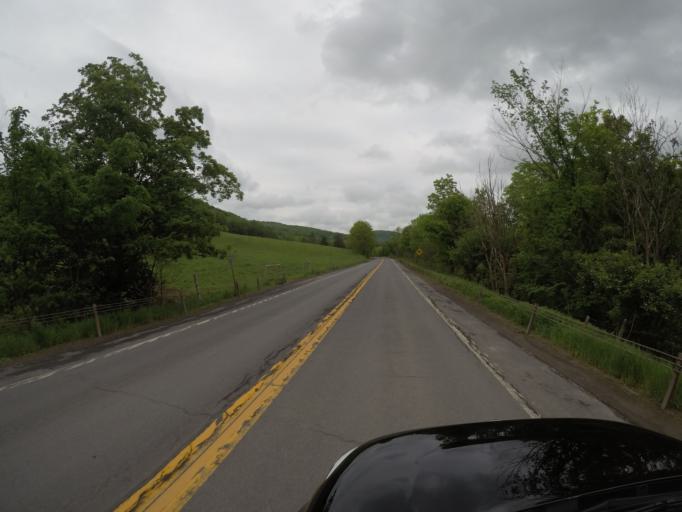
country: US
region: New York
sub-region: Delaware County
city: Delhi
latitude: 42.2578
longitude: -74.8849
